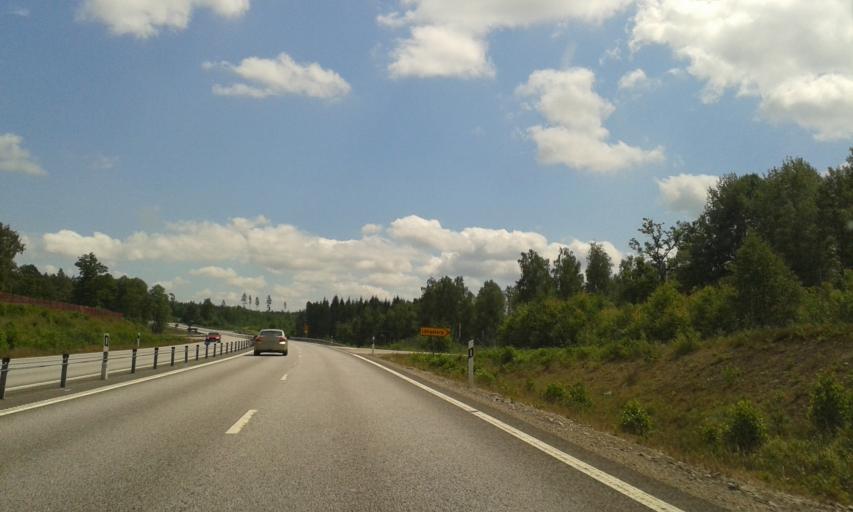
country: SE
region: Kronoberg
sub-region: Vaxjo Kommun
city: Gemla
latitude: 56.8985
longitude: 14.6794
